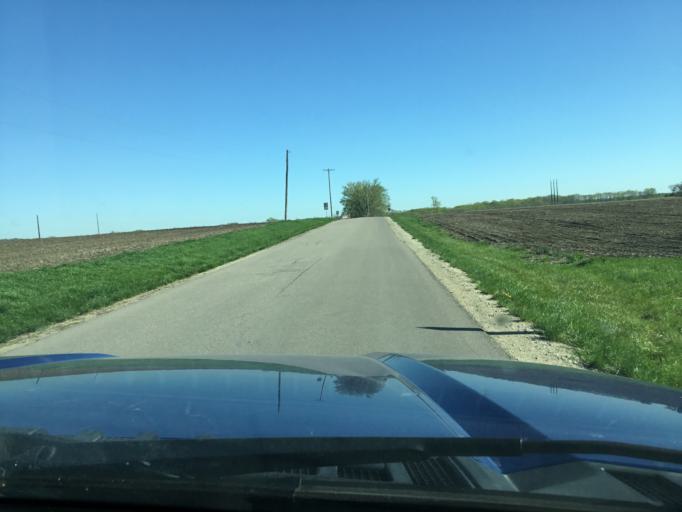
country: US
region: Kansas
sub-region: Douglas County
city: Lawrence
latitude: 38.9991
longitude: -95.3165
